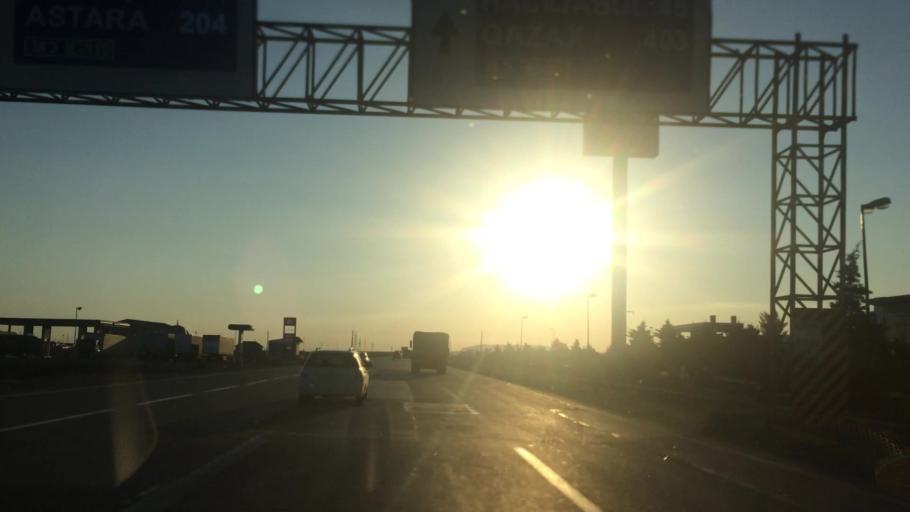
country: AZ
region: Baki
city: Qobustan
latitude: 39.9672
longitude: 49.4093
